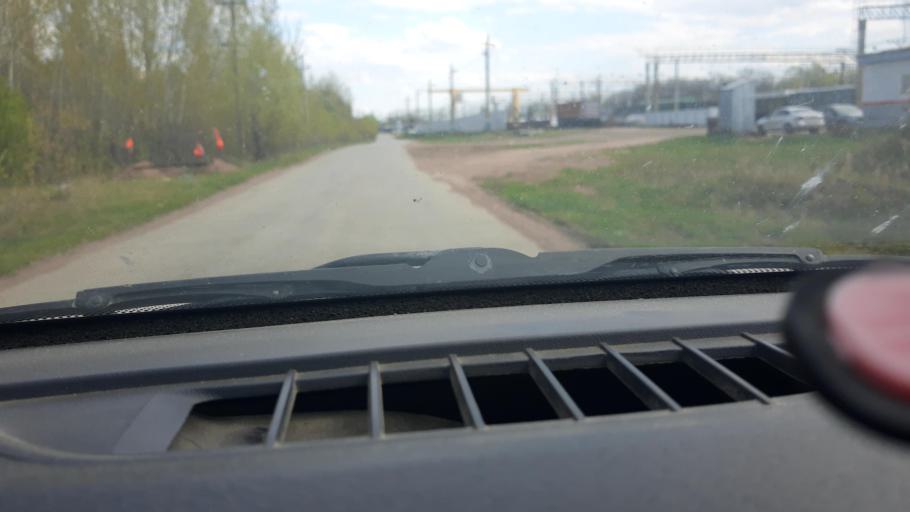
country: RU
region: Bashkortostan
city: Avdon
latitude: 54.6502
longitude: 55.8353
